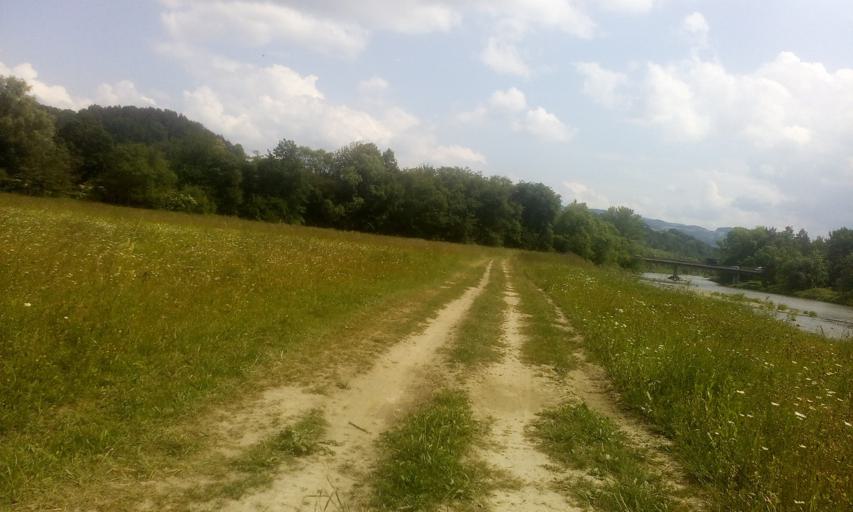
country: PL
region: Lesser Poland Voivodeship
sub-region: Powiat nowosadecki
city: Stary Sacz
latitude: 49.5717
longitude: 20.6574
